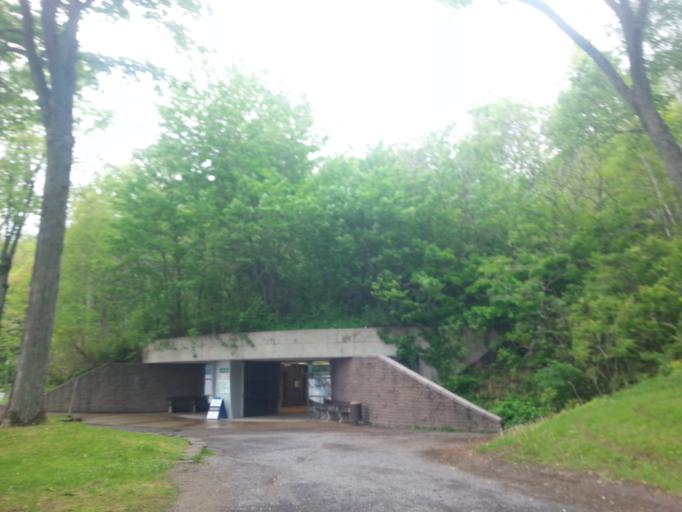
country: CA
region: Quebec
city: L'Ancienne-Lorette
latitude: 46.7505
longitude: -71.3153
